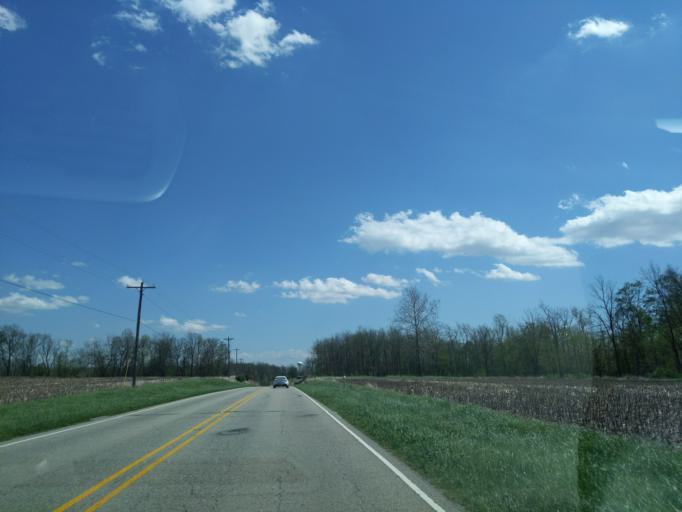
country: US
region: Indiana
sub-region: Decatur County
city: Saint Paul
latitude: 39.3970
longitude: -85.5554
